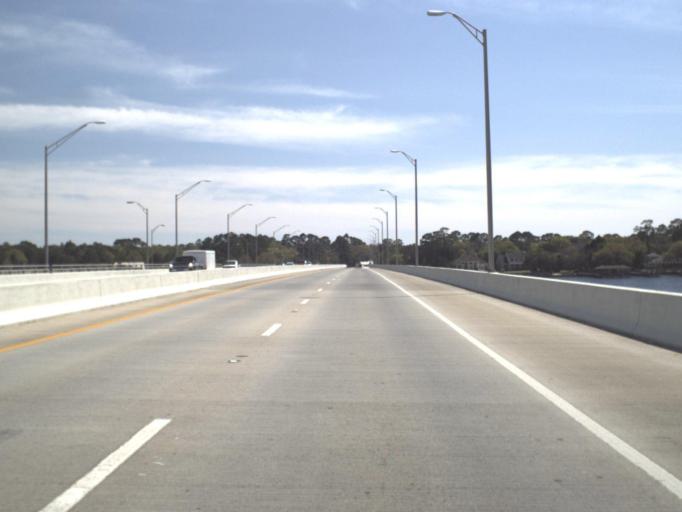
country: US
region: Florida
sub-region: Bay County
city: Lynn Haven
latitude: 30.2591
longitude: -85.6469
